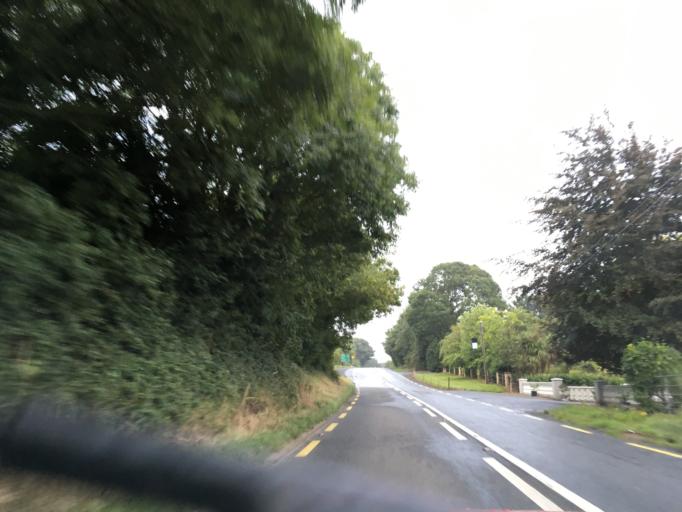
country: IE
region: Munster
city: Tipperary
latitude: 52.4898
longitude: -8.0495
